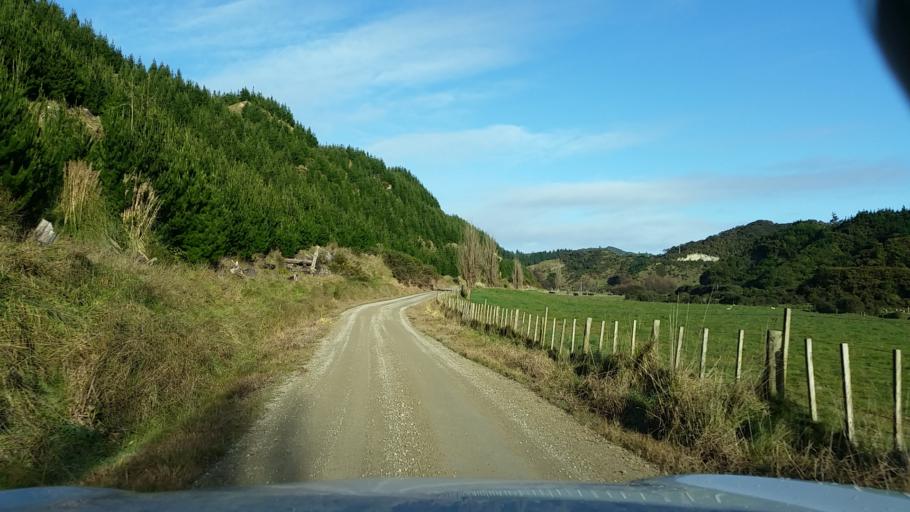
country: NZ
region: Taranaki
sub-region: South Taranaki District
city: Patea
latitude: -39.6946
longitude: 174.7458
